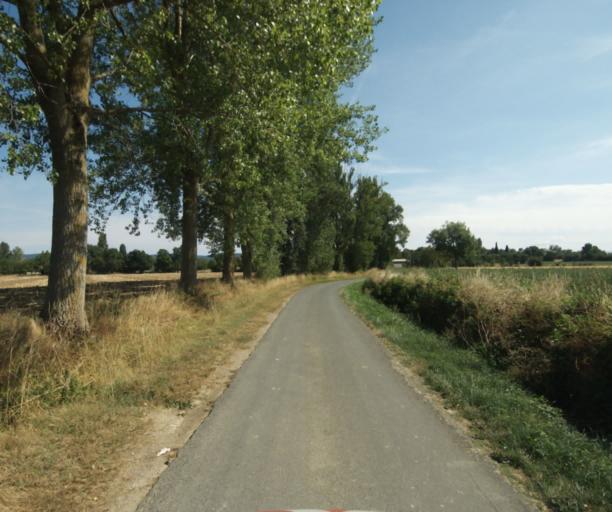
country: FR
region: Midi-Pyrenees
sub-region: Departement de la Haute-Garonne
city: Revel
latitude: 43.4907
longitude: 1.9906
